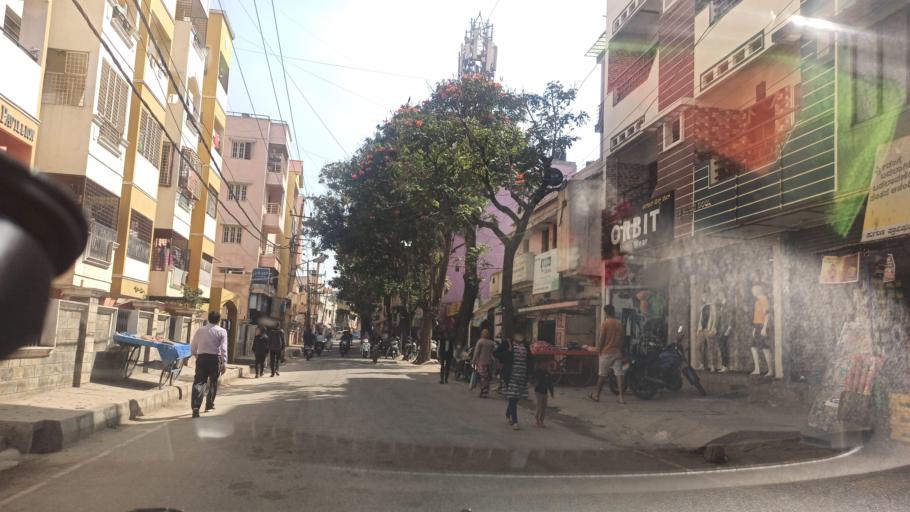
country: IN
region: Karnataka
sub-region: Bangalore Urban
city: Yelahanka
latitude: 13.0400
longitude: 77.5930
